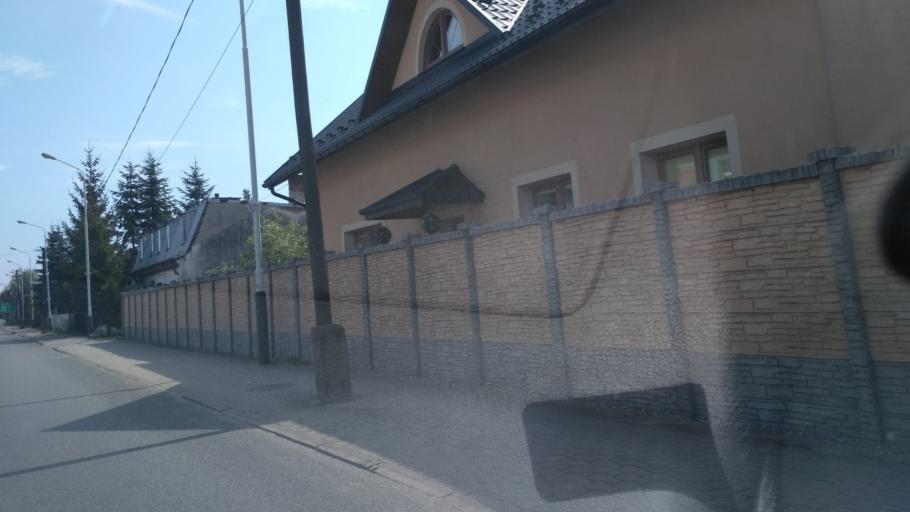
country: PL
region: Subcarpathian Voivodeship
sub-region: Powiat jaroslawski
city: Jaroslaw
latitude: 50.0194
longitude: 22.6933
